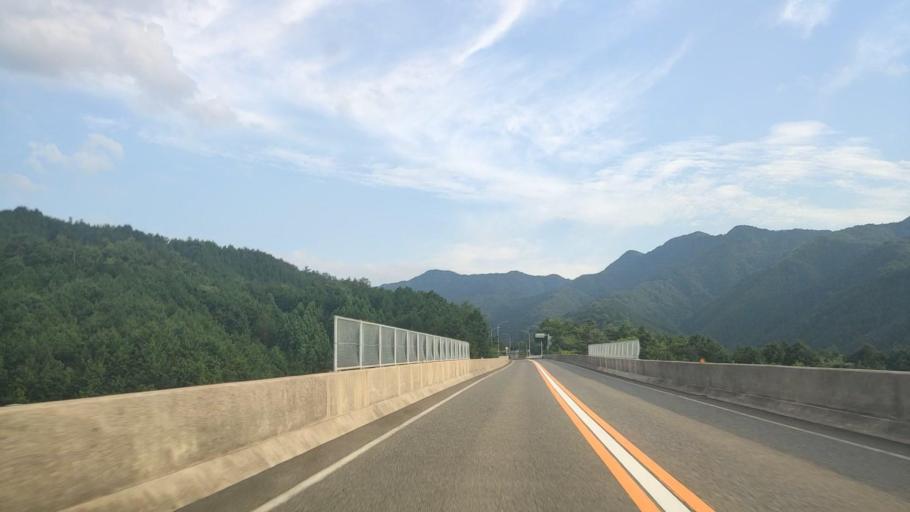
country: JP
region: Tottori
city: Kurayoshi
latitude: 35.3319
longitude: 133.7551
